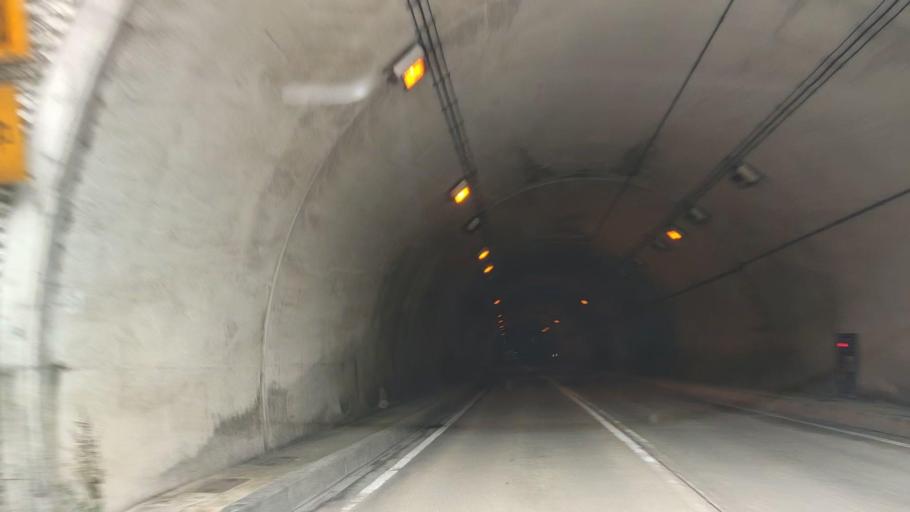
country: JP
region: Kyoto
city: Fukuchiyama
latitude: 35.2113
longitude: 134.9427
